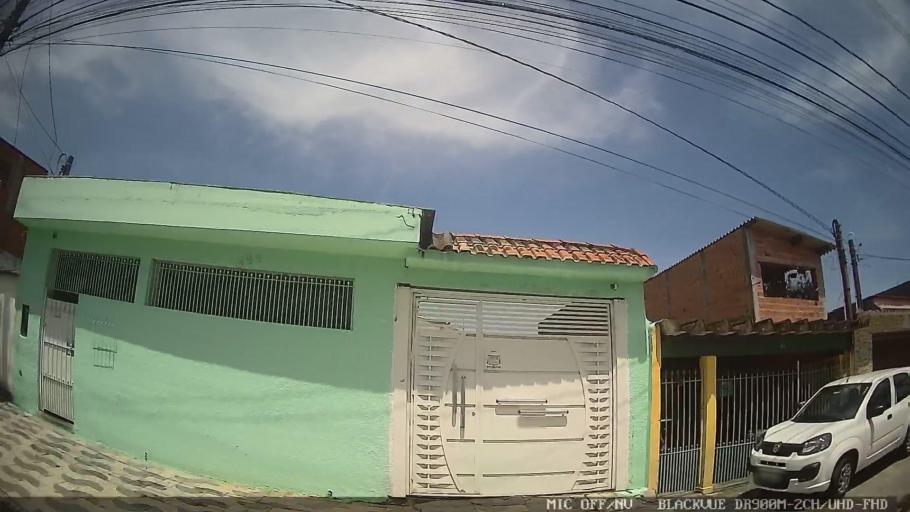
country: BR
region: Sao Paulo
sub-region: Suzano
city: Suzano
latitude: -23.5199
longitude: -46.3046
